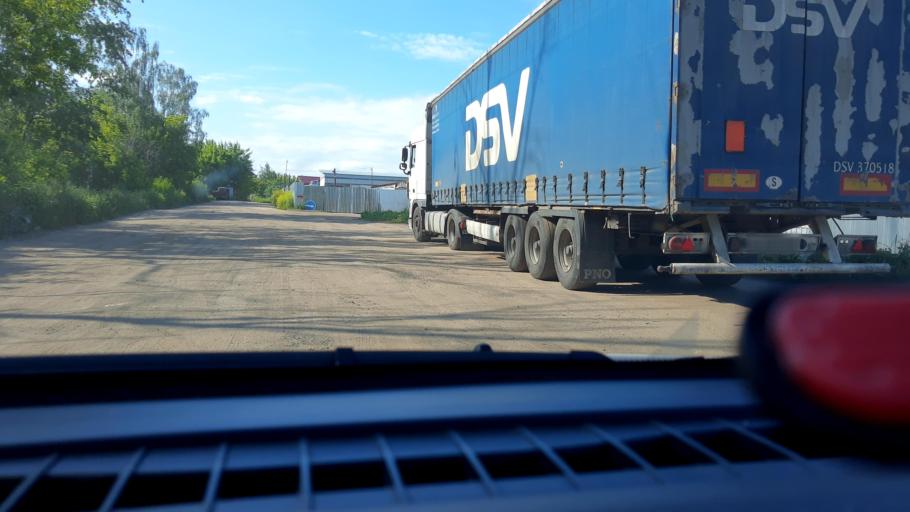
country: RU
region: Nizjnij Novgorod
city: Kstovo
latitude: 56.1975
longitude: 44.1526
